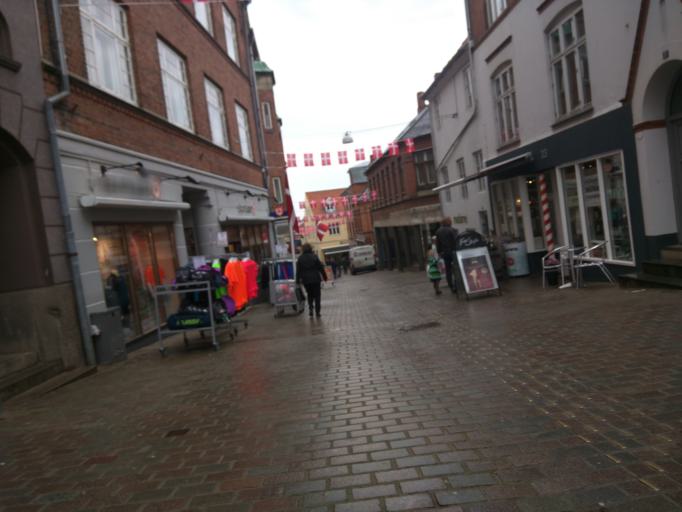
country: DK
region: Central Jutland
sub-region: Viborg Kommune
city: Viborg
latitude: 56.4506
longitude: 9.4094
